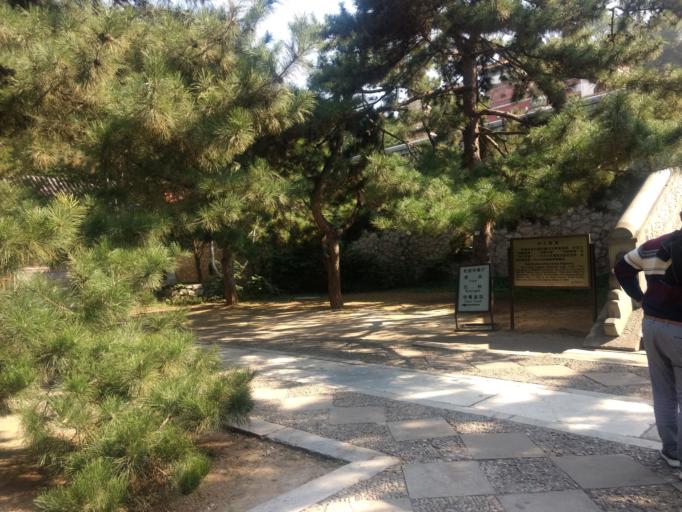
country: CN
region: Beijing
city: Haidian
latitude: 39.9998
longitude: 116.2682
